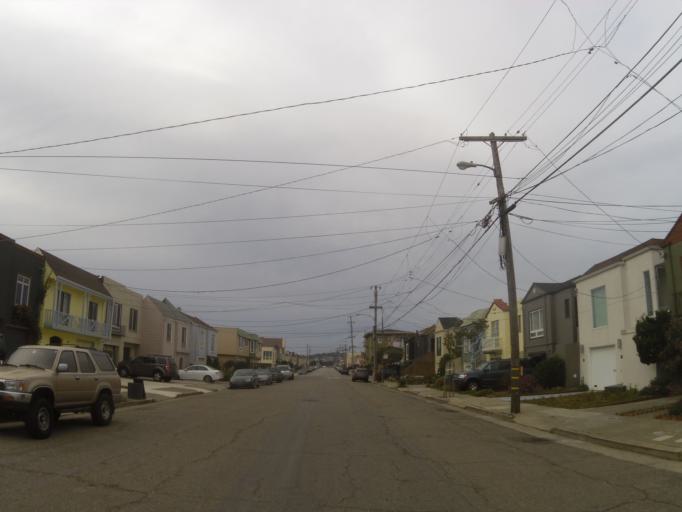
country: US
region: California
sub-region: San Mateo County
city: Daly City
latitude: 37.7502
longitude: -122.5063
